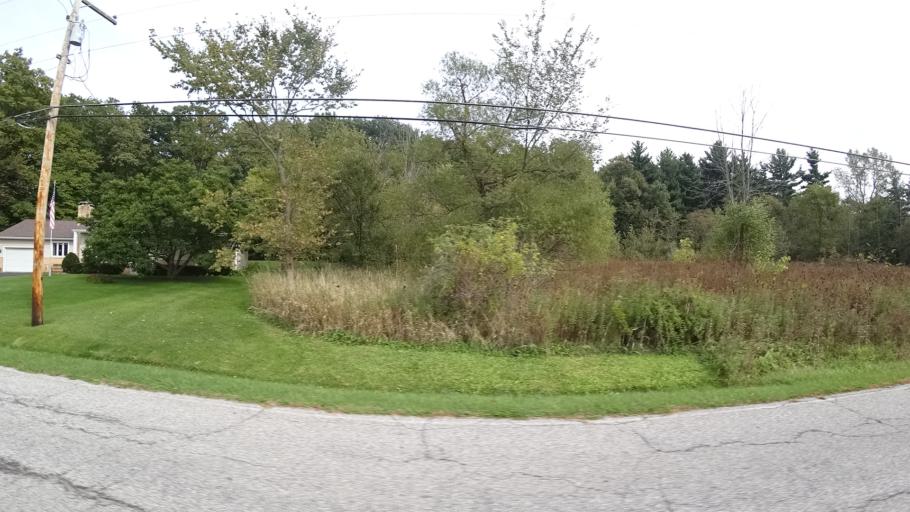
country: US
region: Indiana
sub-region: LaPorte County
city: Trail Creek
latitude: 41.7046
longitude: -86.8163
